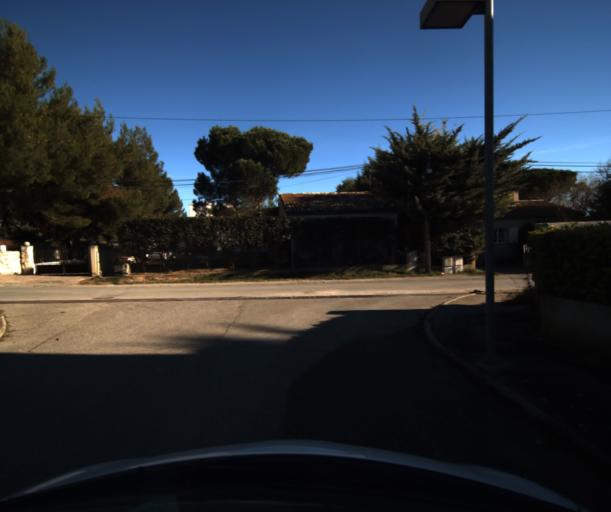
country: FR
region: Provence-Alpes-Cote d'Azur
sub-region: Departement du Vaucluse
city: Pertuis
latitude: 43.6991
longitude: 5.4820
